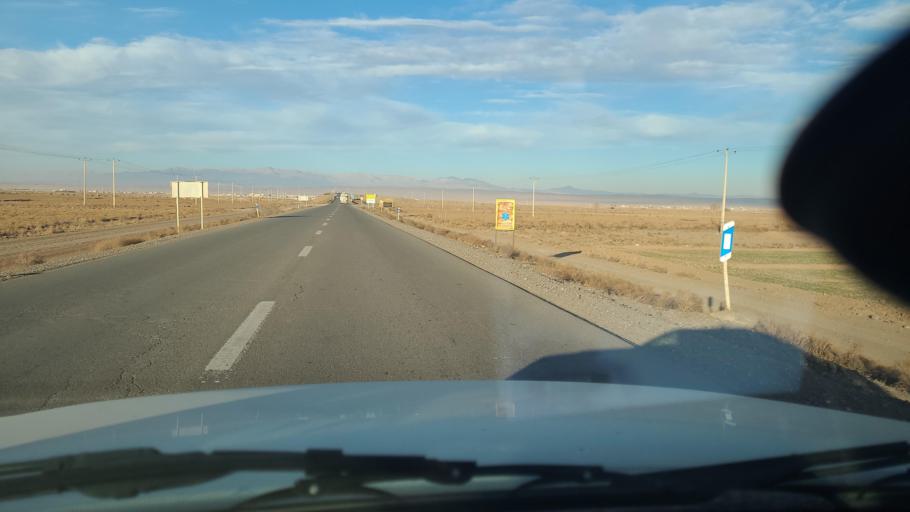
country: IR
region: Razavi Khorasan
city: Neqab
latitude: 36.5974
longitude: 57.5878
